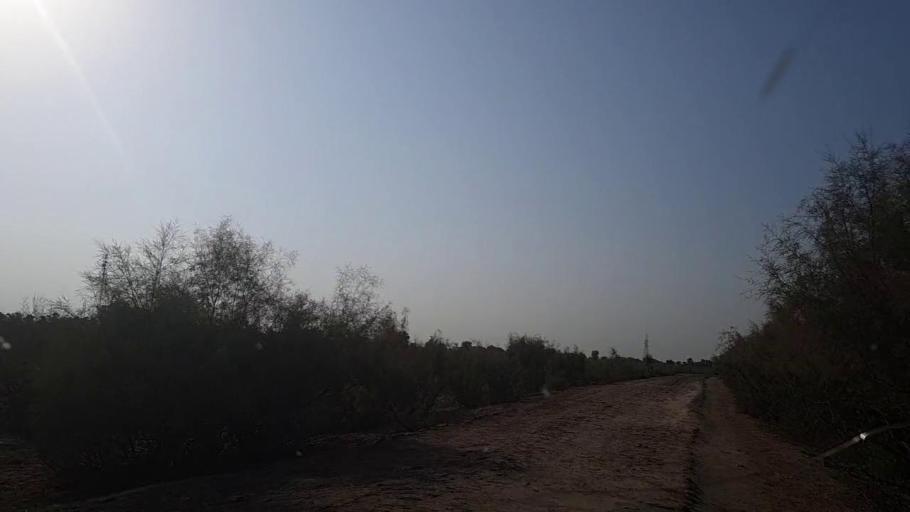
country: PK
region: Sindh
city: Khanpur
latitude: 27.7262
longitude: 69.3082
